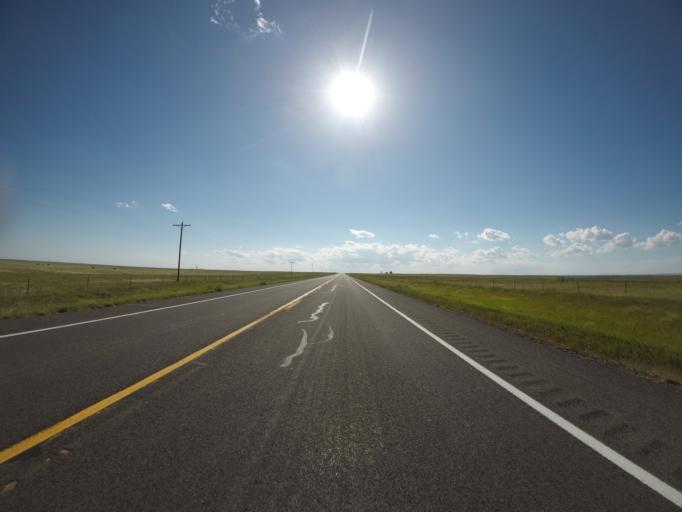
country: US
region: Colorado
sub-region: Morgan County
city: Brush
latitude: 40.6102
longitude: -103.6484
